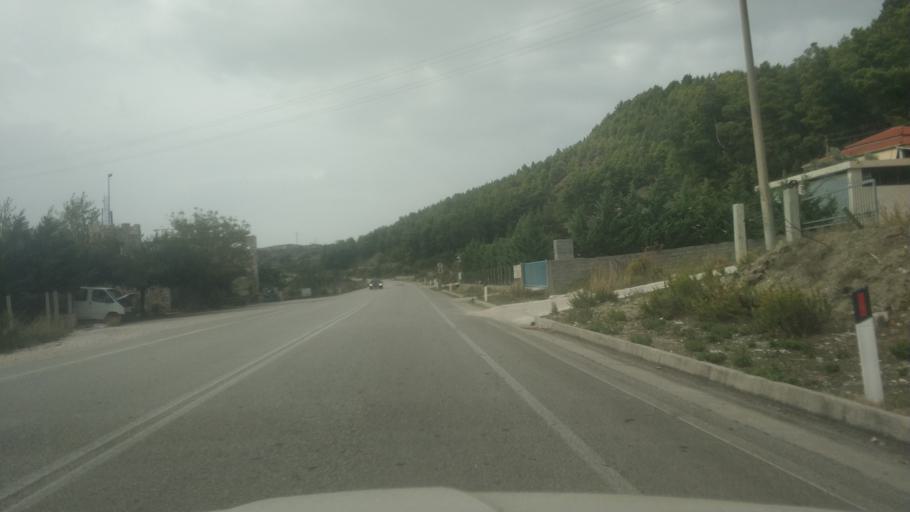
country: AL
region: Gjirokaster
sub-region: Rrethi i Tepelenes
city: Memaliaj
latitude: 40.3536
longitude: 19.9509
